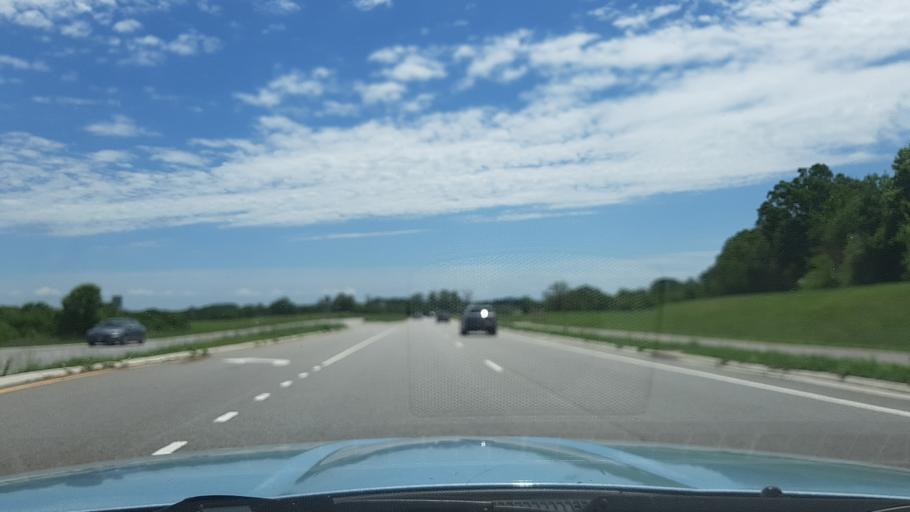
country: US
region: Virginia
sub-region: Fairfax County
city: Lorton
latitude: 38.7077
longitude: -77.2554
